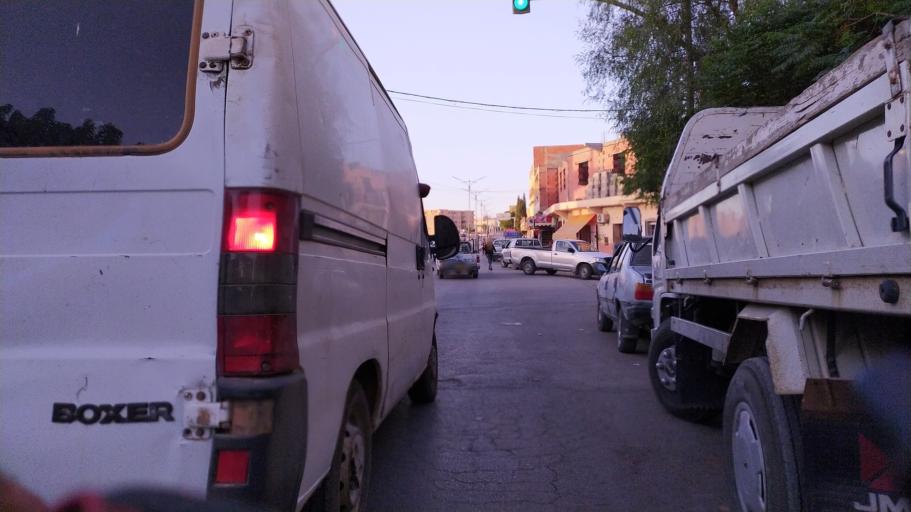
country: DZ
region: Tiaret
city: Frenda
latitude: 34.8940
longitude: 1.2470
